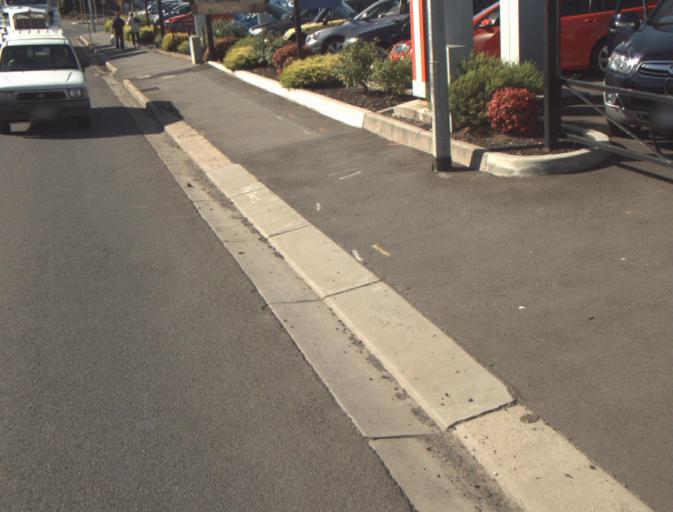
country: AU
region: Tasmania
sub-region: Launceston
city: Launceston
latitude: -41.4333
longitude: 147.1335
